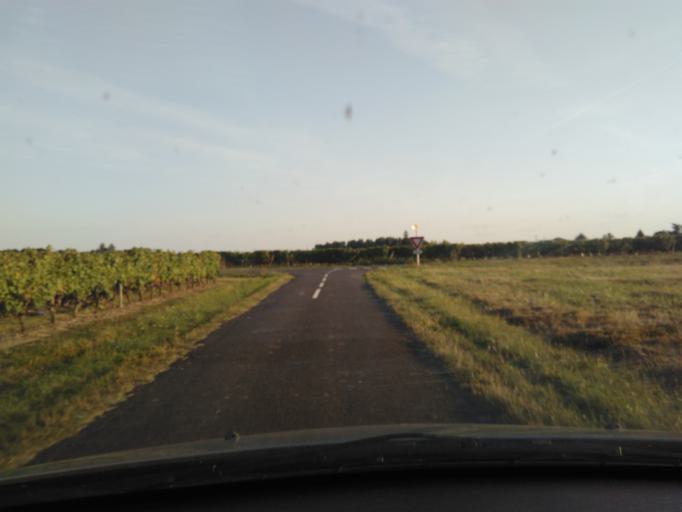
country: FR
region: Pays de la Loire
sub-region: Departement de Maine-et-Loire
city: Saint-Saturnin-sur-Loire
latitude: 47.3884
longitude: -0.4170
